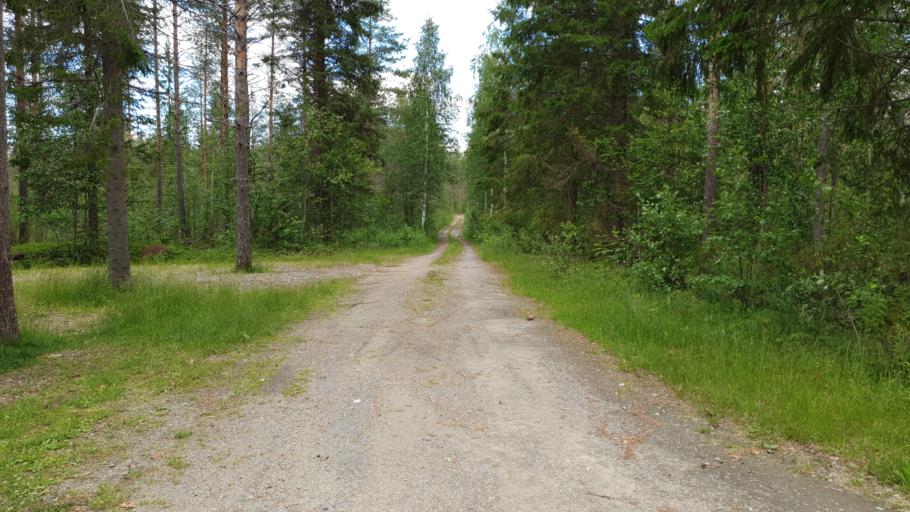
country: FI
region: Kainuu
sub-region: Kehys-Kainuu
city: Kuhmo
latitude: 64.0378
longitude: 29.5767
